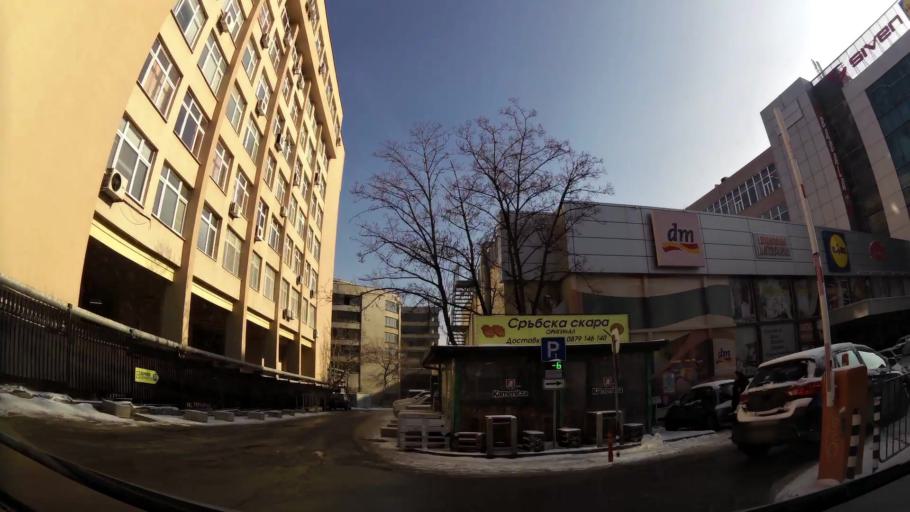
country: BG
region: Sofia-Capital
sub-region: Stolichna Obshtina
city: Sofia
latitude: 42.6629
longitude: 23.3176
